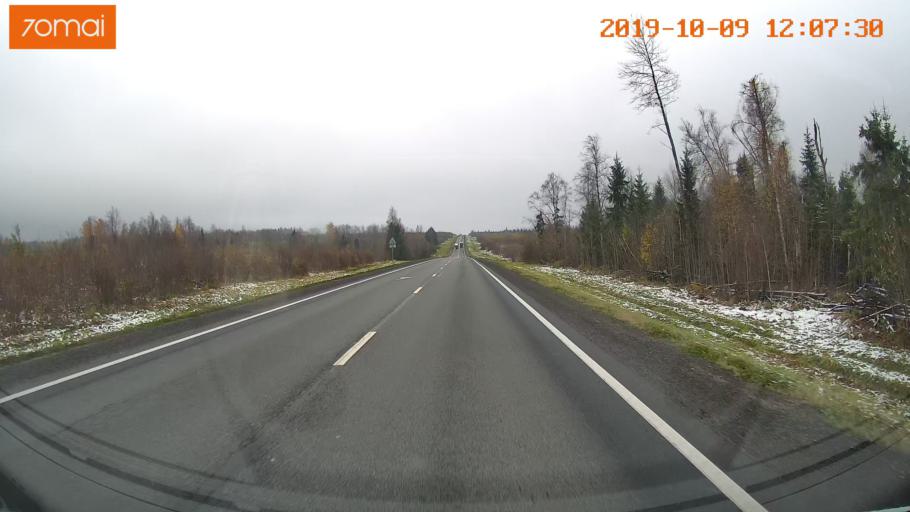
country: RU
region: Jaroslavl
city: Prechistoye
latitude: 58.5986
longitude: 40.3423
